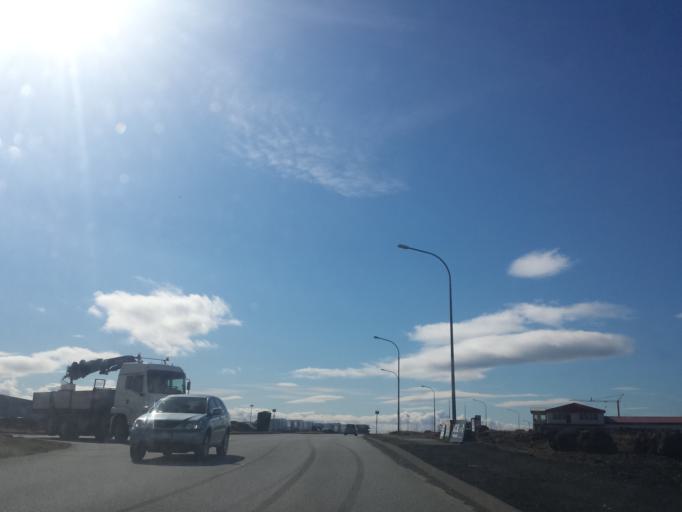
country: IS
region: Capital Region
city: Gardabaer
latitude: 64.0778
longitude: -21.9283
